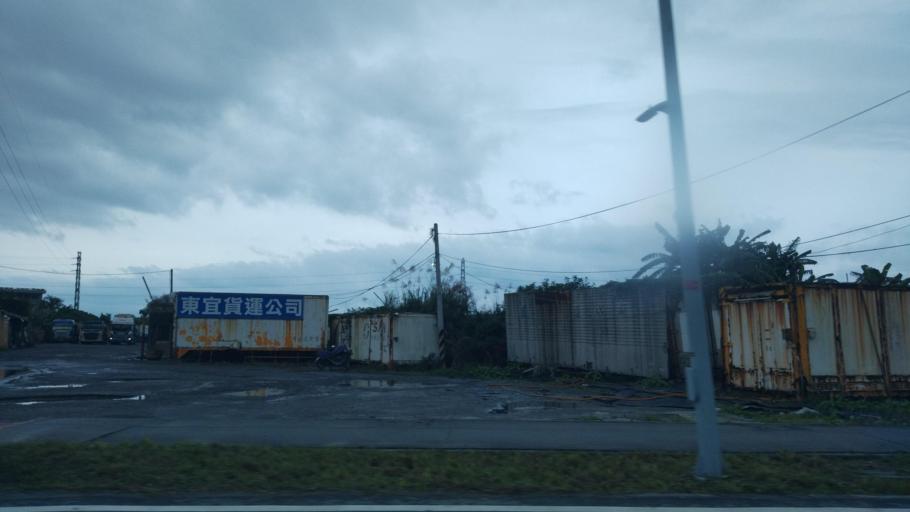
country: TW
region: Taiwan
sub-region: Yilan
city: Yilan
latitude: 24.6141
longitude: 121.8303
